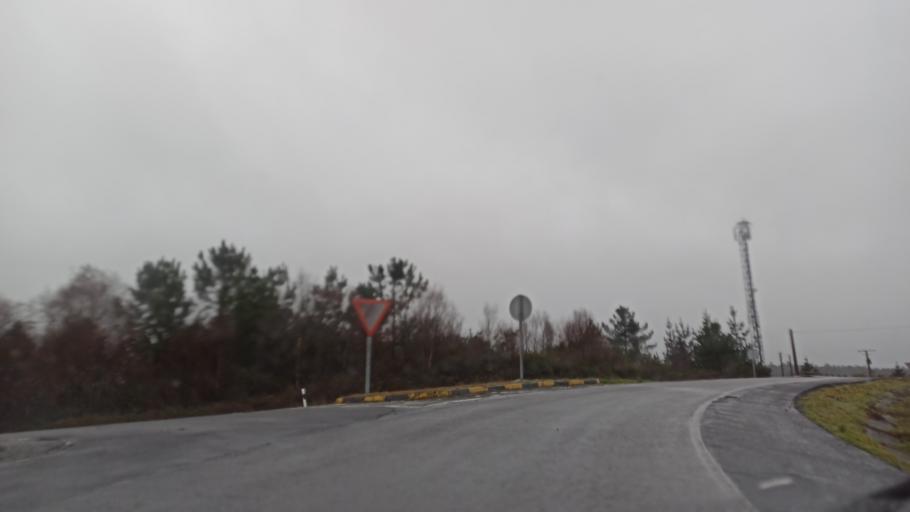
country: ES
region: Galicia
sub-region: Provincia de Lugo
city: Guitiriz
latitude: 43.1936
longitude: -7.9603
